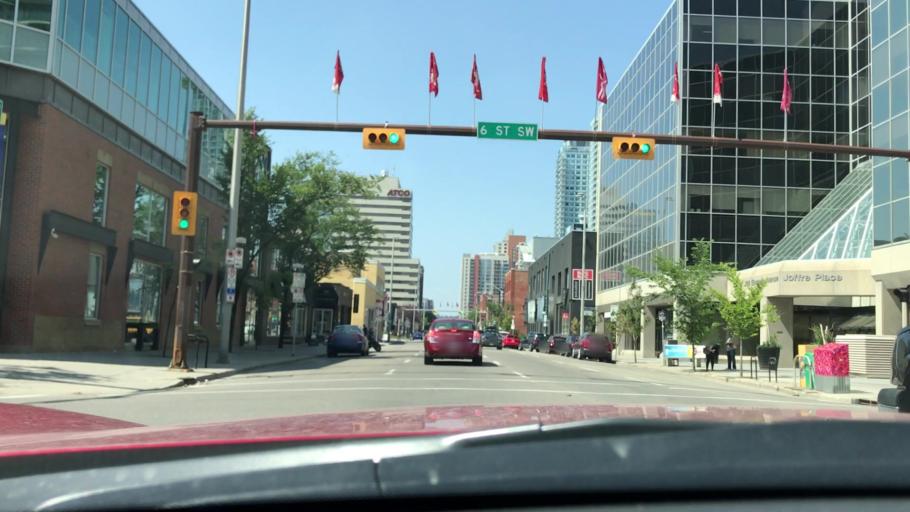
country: CA
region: Alberta
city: Calgary
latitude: 51.0428
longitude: -114.0765
